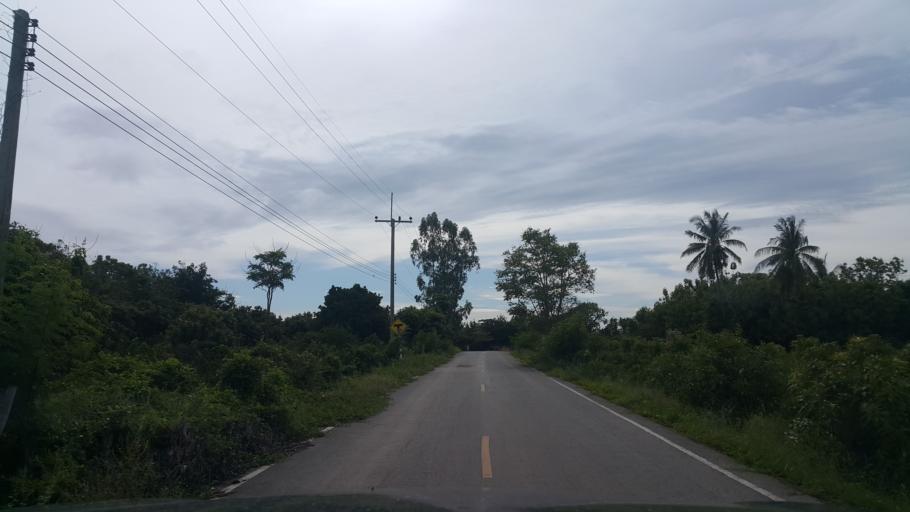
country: TH
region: Sukhothai
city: Si Nakhon
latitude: 17.2683
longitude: 99.9251
